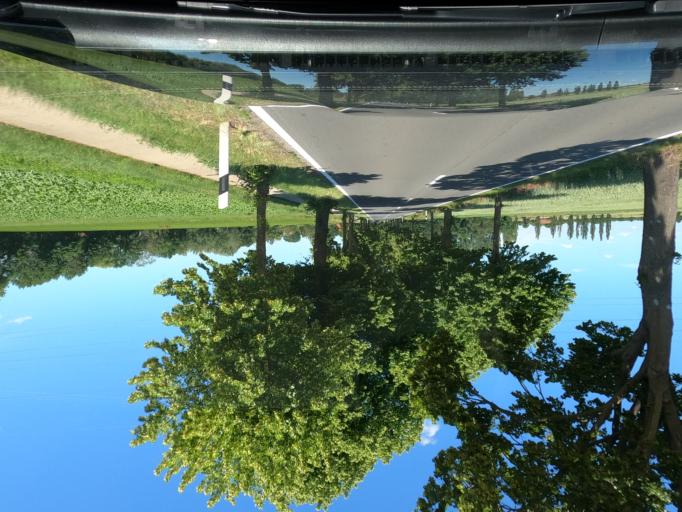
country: DE
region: Lower Saxony
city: Lehrte
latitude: 52.4109
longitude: 9.9757
